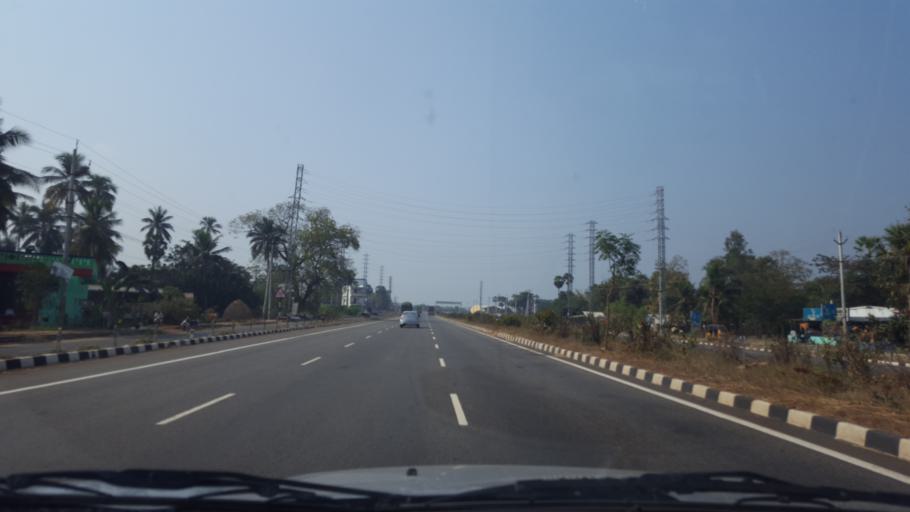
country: IN
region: Andhra Pradesh
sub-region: Vizianagaram District
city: Vizianagaram
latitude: 18.0249
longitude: 83.4897
